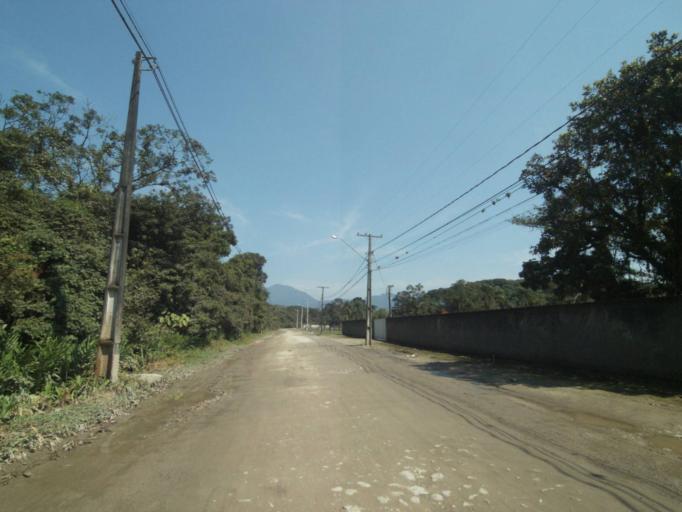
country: BR
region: Parana
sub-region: Paranagua
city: Paranagua
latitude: -25.5519
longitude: -48.5881
